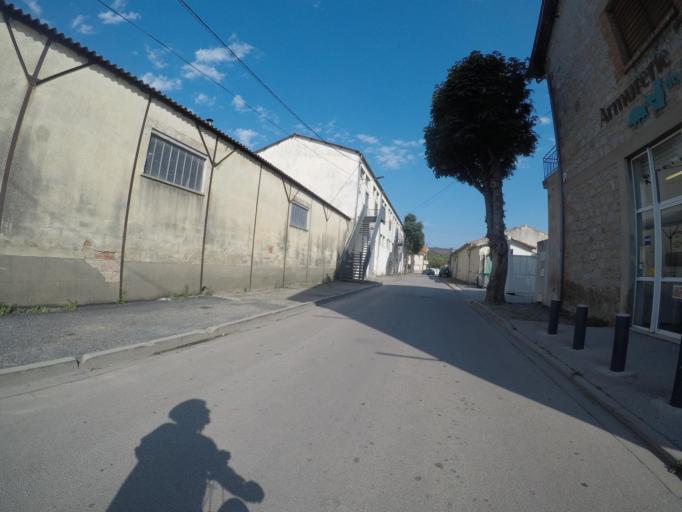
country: FR
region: Languedoc-Roussillon
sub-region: Departement des Pyrenees-Orientales
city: Ille-sur-Tet
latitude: 42.6726
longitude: 2.6245
